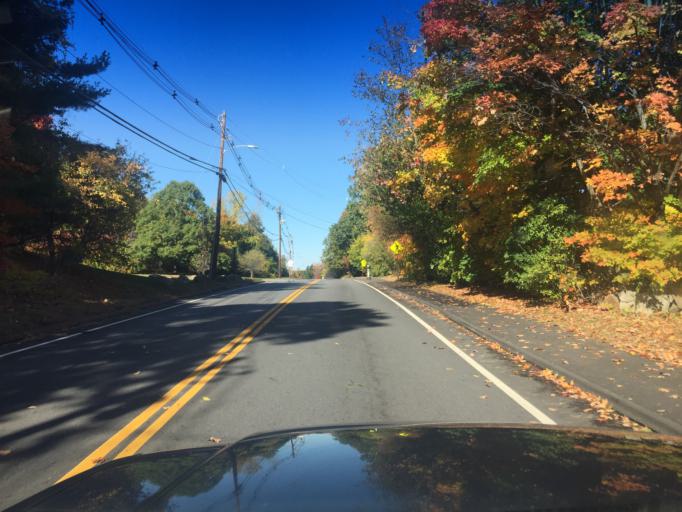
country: US
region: Massachusetts
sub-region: Middlesex County
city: Hudson
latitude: 42.3804
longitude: -71.5490
